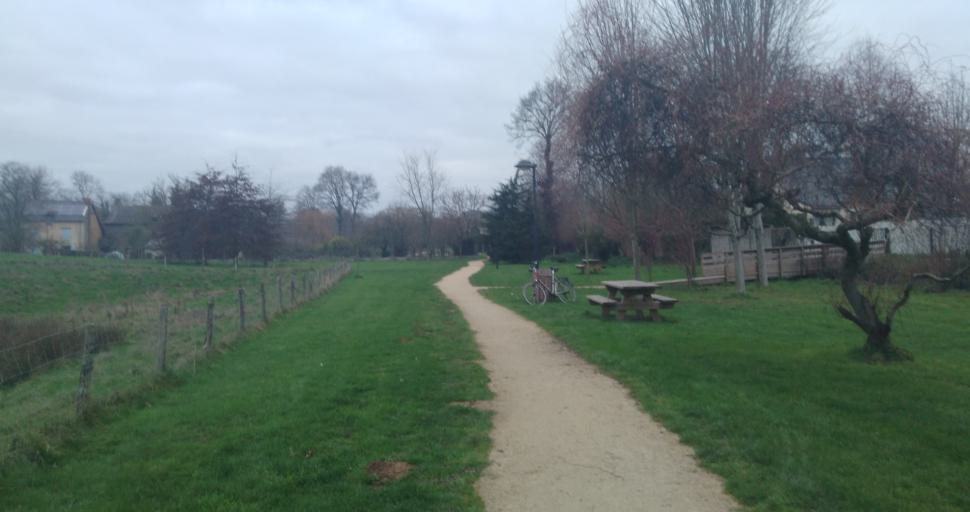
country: FR
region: Brittany
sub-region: Departement d'Ille-et-Vilaine
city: Romille
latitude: 48.2158
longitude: -1.8946
